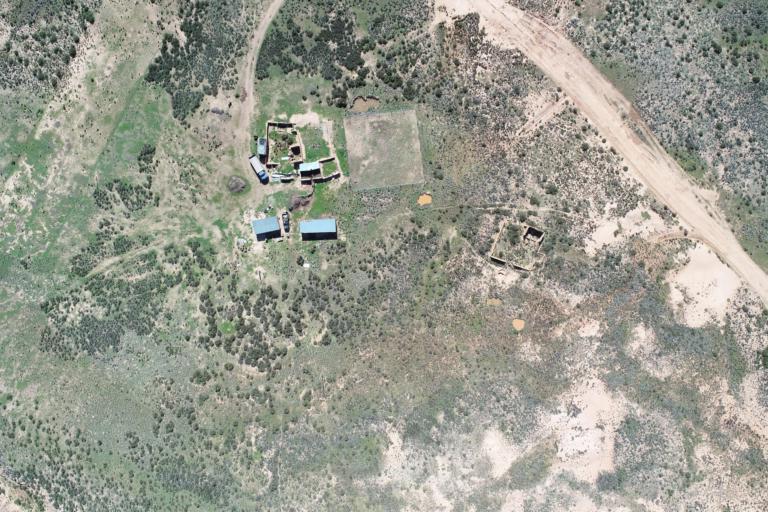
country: BO
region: La Paz
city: Curahuara de Carangas
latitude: -17.2932
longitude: -68.5118
